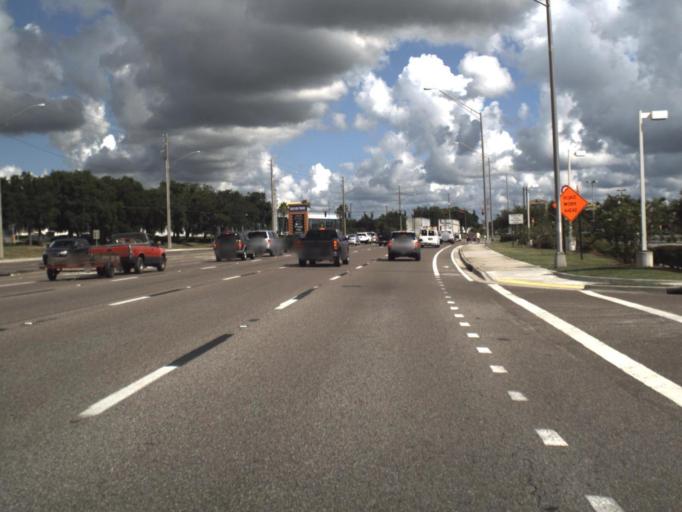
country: US
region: Florida
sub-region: Polk County
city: Gibsonia
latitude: 28.0898
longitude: -81.9733
